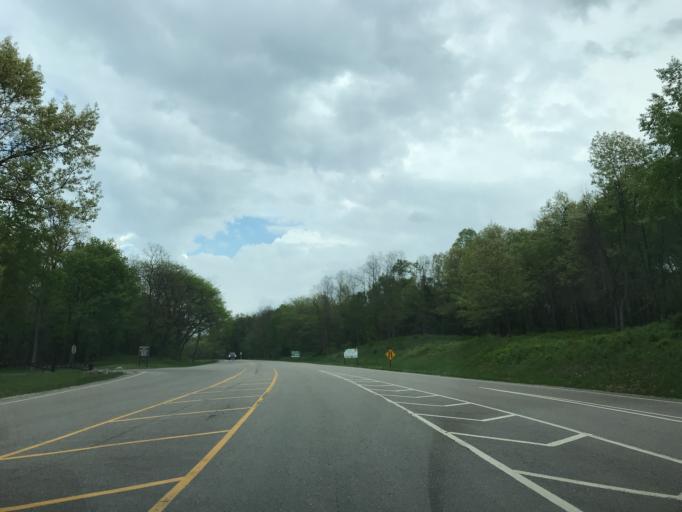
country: US
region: Michigan
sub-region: Oakland County
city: South Lyon
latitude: 42.5210
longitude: -83.6440
